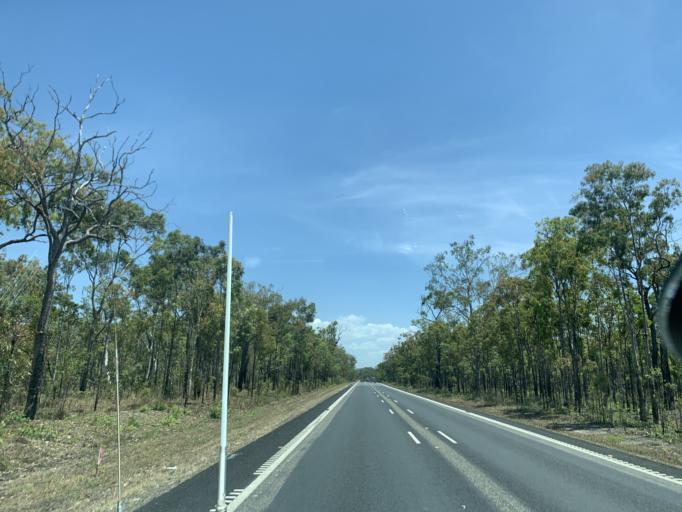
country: AU
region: Queensland
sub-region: Tablelands
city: Kuranda
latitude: -16.9280
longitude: 145.5483
